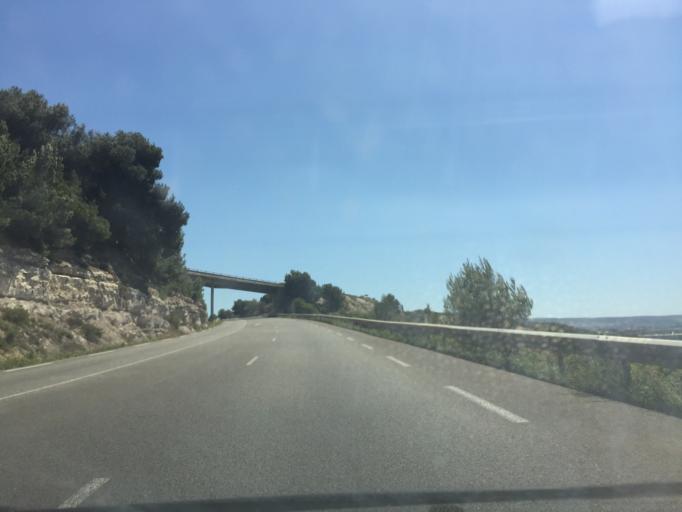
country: FR
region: Provence-Alpes-Cote d'Azur
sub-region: Departement des Bouches-du-Rhone
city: Vitrolles
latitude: 43.4471
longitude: 5.2388
